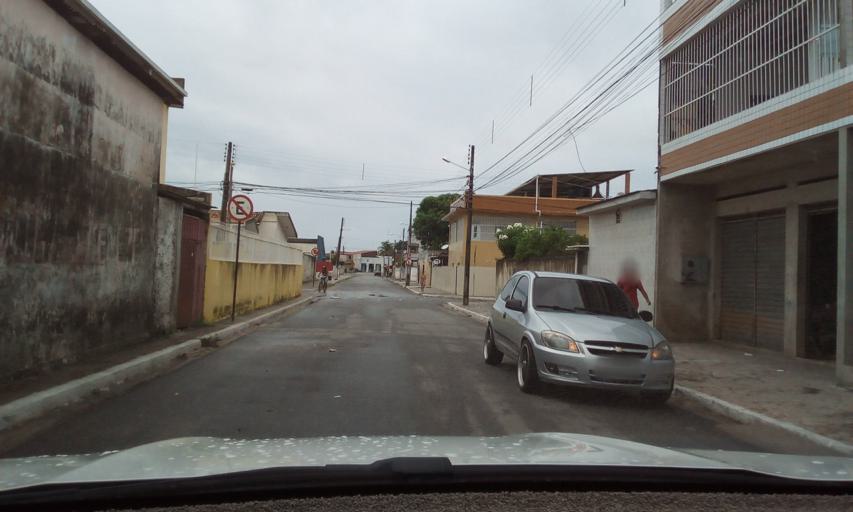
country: BR
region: Paraiba
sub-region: Joao Pessoa
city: Joao Pessoa
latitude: -7.1668
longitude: -34.8361
